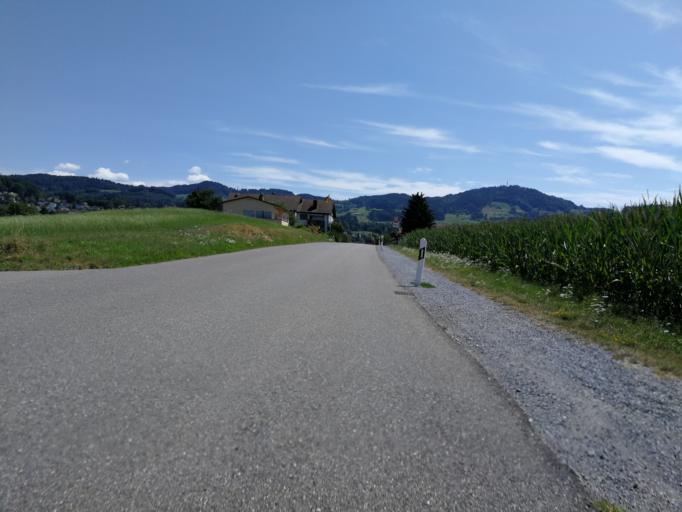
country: CH
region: Zurich
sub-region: Bezirk Hinwil
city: Hinwil
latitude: 47.2977
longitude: 8.8329
